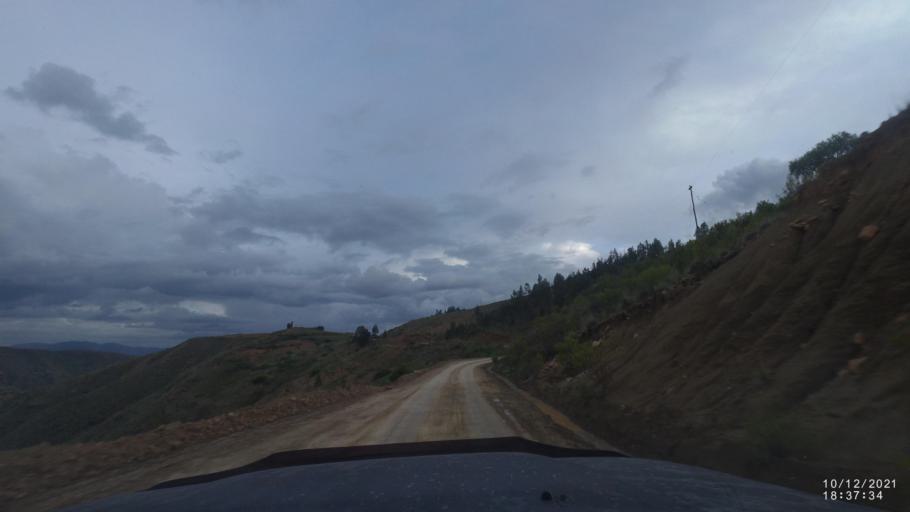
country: BO
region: Cochabamba
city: Tarata
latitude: -17.8383
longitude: -65.9925
